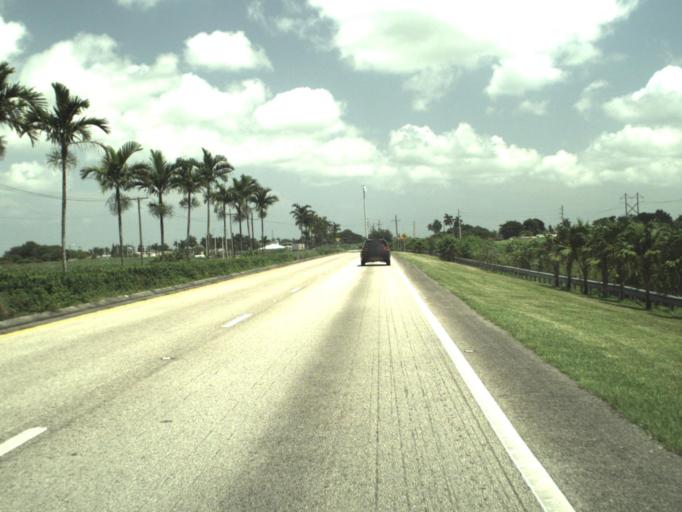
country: US
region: Florida
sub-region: Palm Beach County
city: South Bay
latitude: 26.6543
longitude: -80.7125
